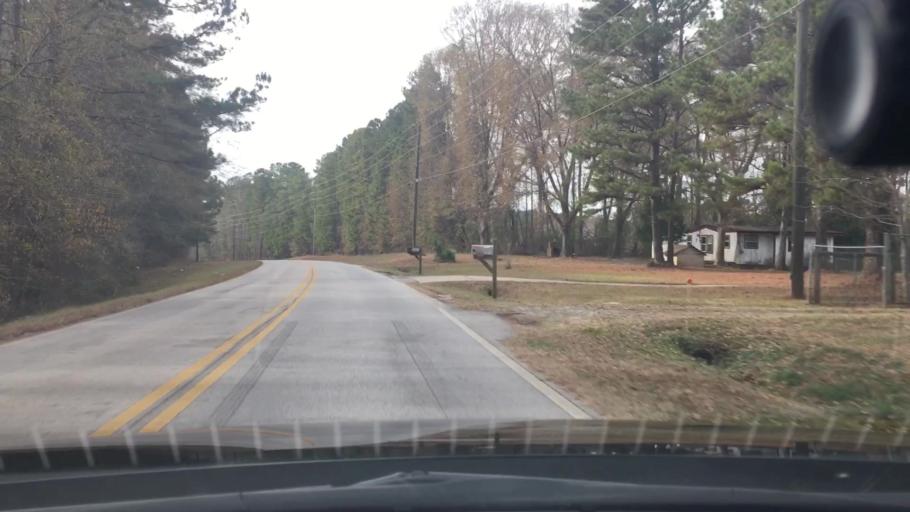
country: US
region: Georgia
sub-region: Spalding County
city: Experiment
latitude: 33.2761
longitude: -84.3267
